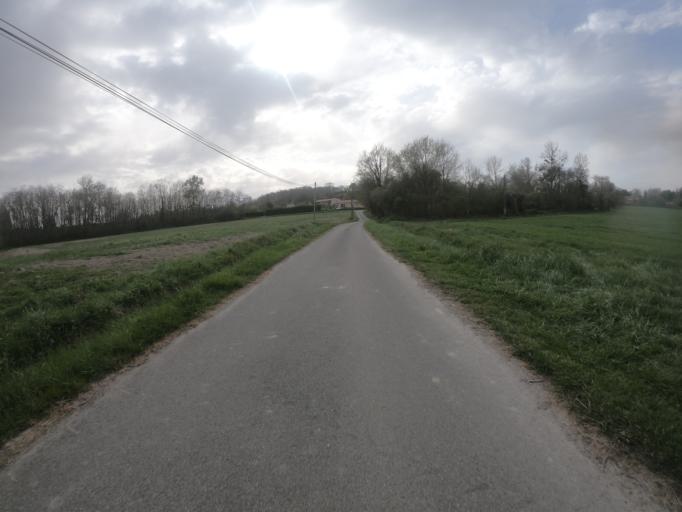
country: FR
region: Midi-Pyrenees
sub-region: Departement de l'Ariege
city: La Tour-du-Crieu
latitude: 43.1012
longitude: 1.7185
